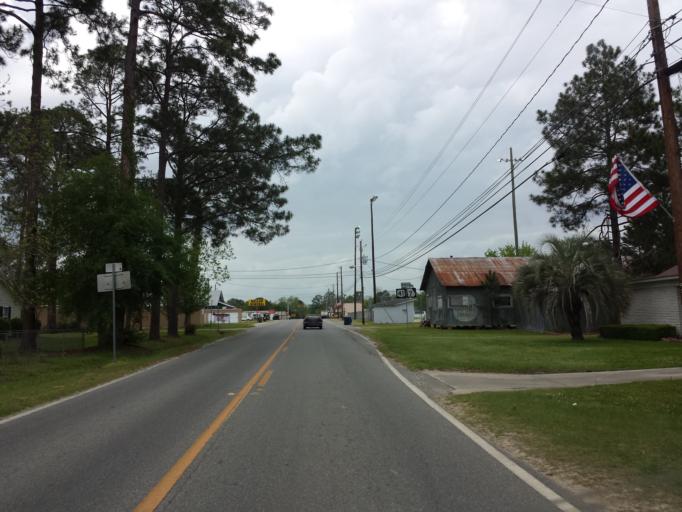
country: US
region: Georgia
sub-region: Cook County
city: Sparks
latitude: 31.2693
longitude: -83.4645
